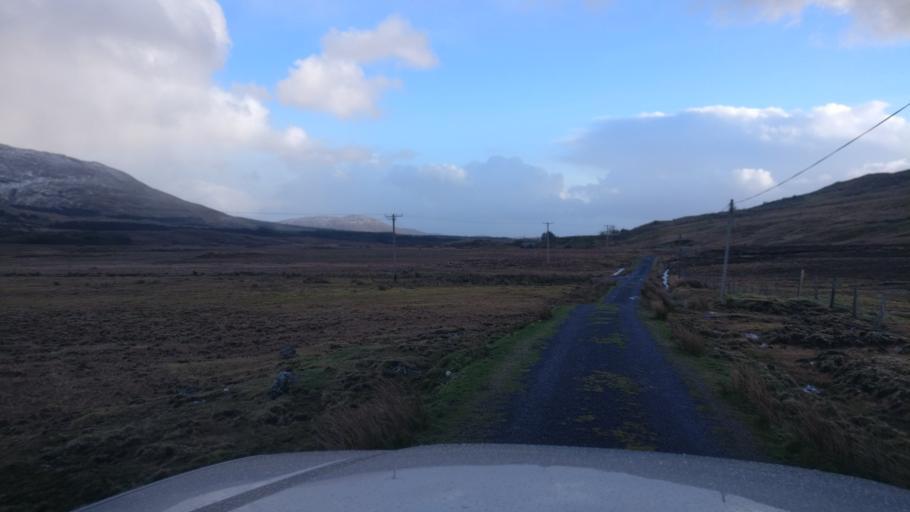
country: IE
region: Connaught
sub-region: County Galway
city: Clifden
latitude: 53.4959
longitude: -9.7047
